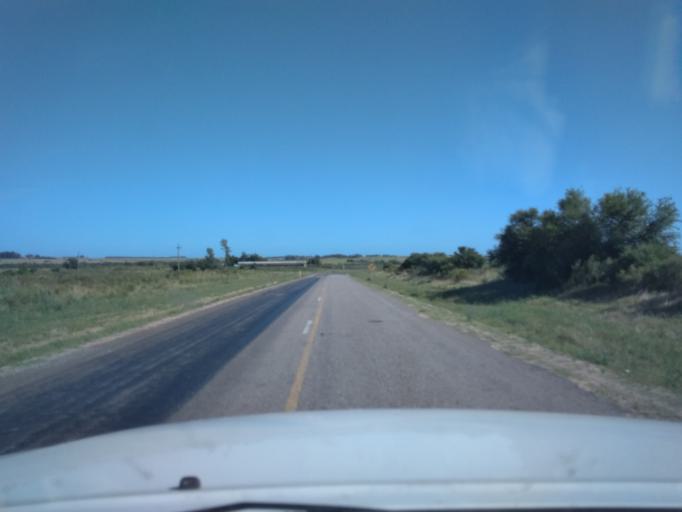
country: UY
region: Canelones
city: San Ramon
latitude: -34.2251
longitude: -55.9304
